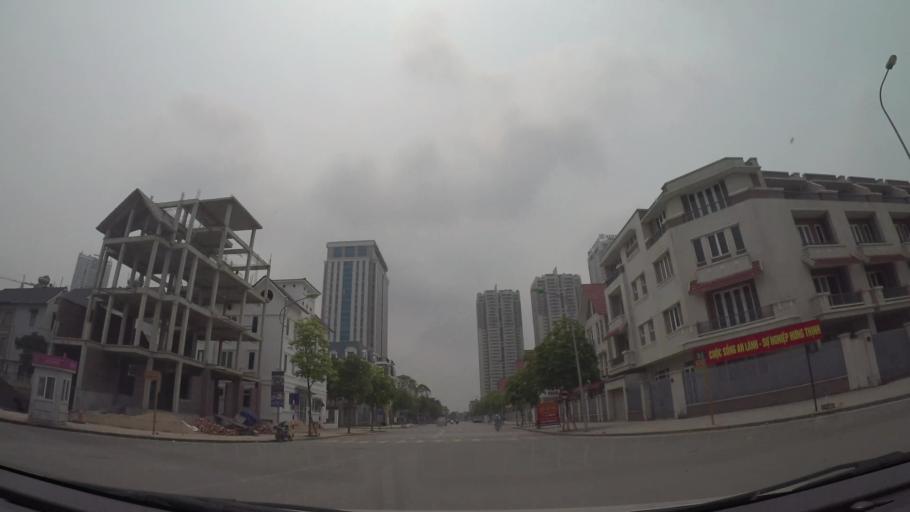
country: VN
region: Ha Noi
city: Ha Dong
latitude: 20.9758
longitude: 105.7564
